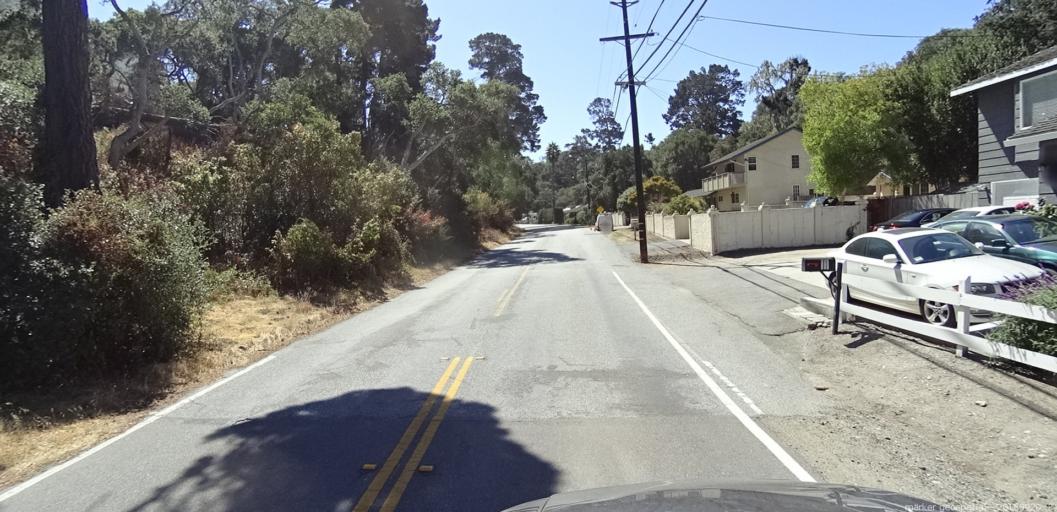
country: US
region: California
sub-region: Monterey County
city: Monterey
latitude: 36.5907
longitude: -121.8700
